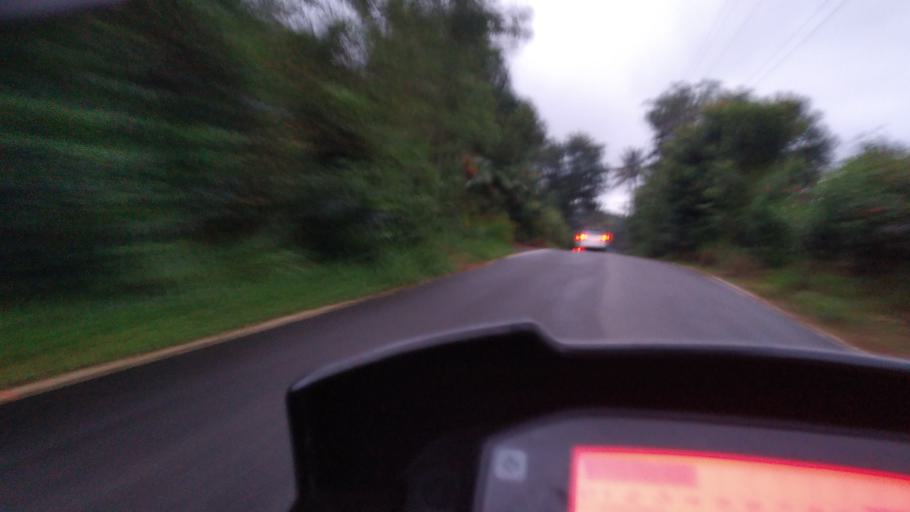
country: IN
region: Kerala
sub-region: Idukki
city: Munnar
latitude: 9.9584
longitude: 77.0910
